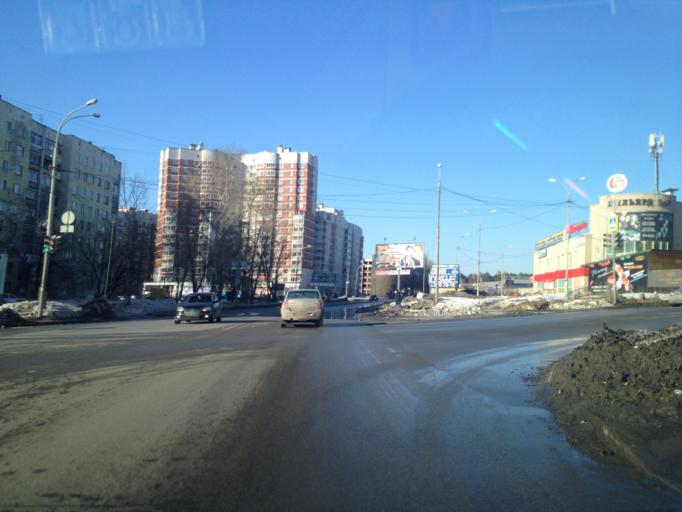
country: RU
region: Sverdlovsk
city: Yekaterinburg
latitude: 56.9077
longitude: 60.6205
